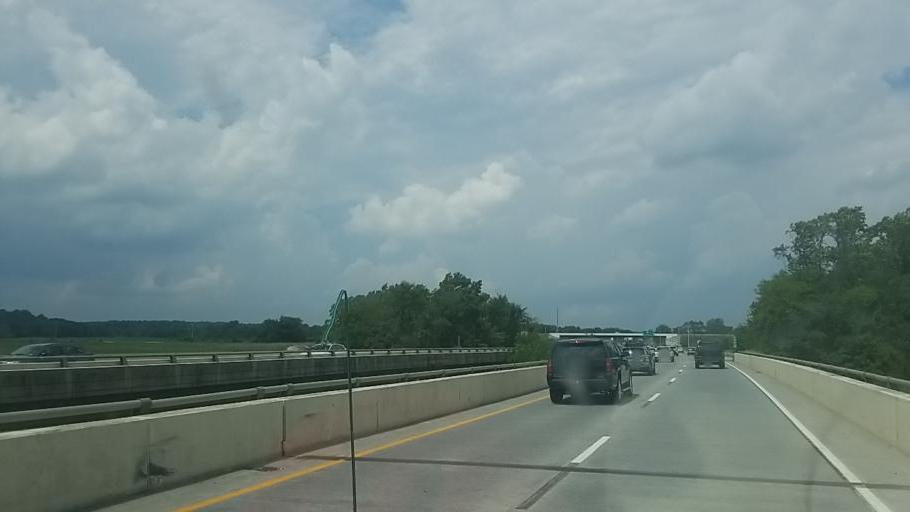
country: US
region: Delaware
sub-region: Kent County
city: Riverview
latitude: 39.0115
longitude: -75.4589
